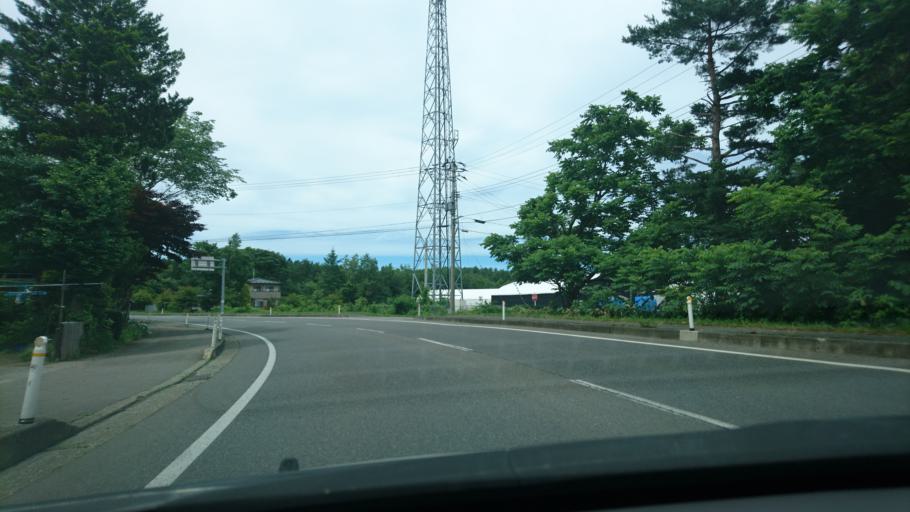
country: JP
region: Iwate
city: Miyako
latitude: 39.9149
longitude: 141.9052
